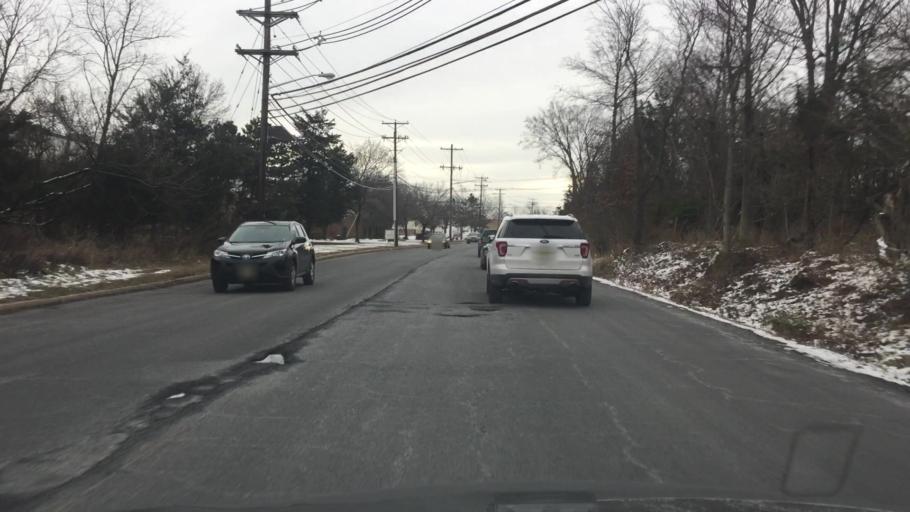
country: US
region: New Jersey
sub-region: Middlesex County
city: Edison
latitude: 40.5280
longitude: -74.4344
